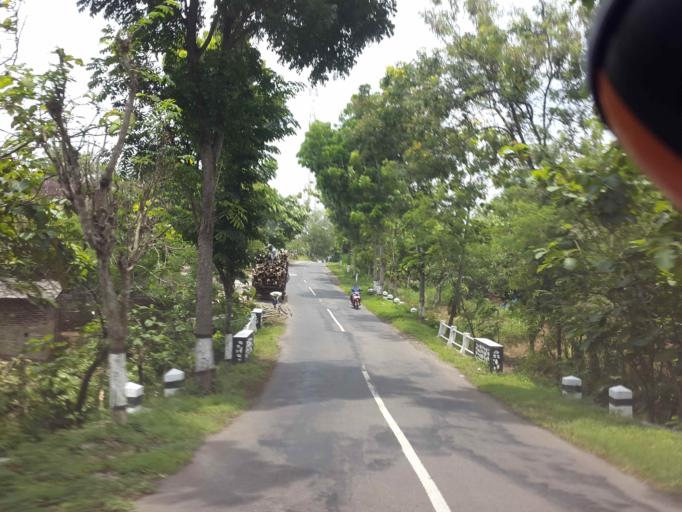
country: ID
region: East Java
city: Ponorogo
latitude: -7.7197
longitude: 111.3575
